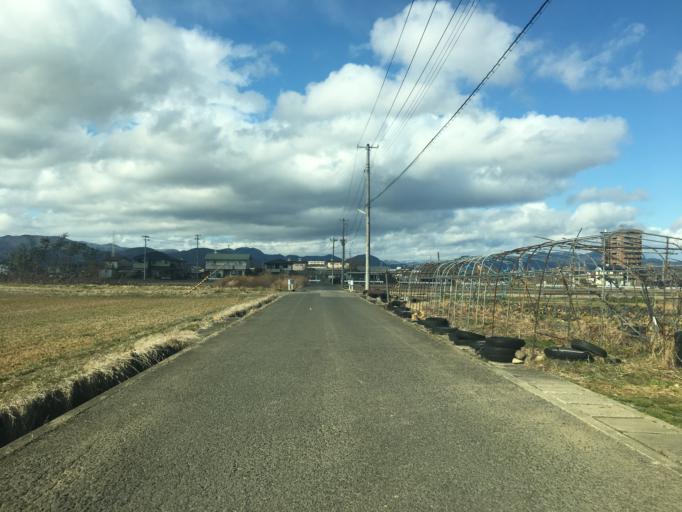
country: JP
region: Fukushima
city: Fukushima-shi
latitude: 37.7498
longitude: 140.4327
